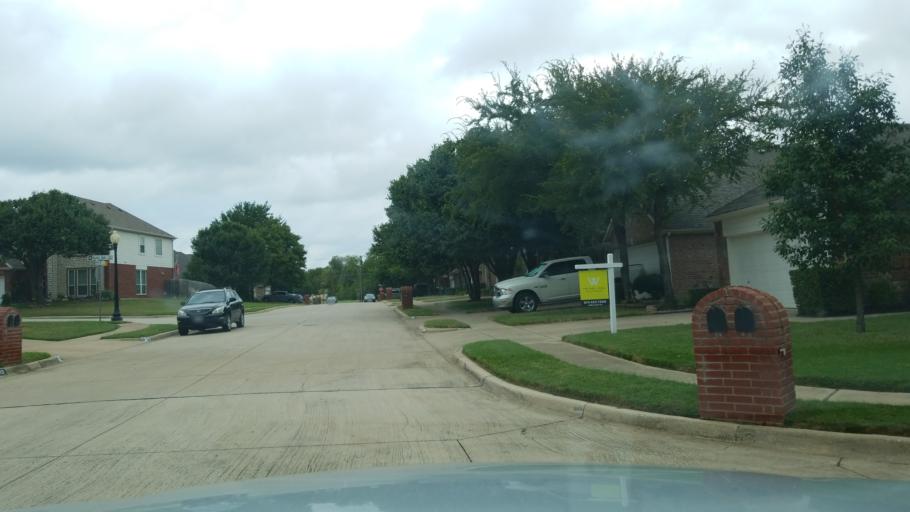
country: US
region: Texas
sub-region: Tarrant County
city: Euless
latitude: 32.8427
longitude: -97.1013
